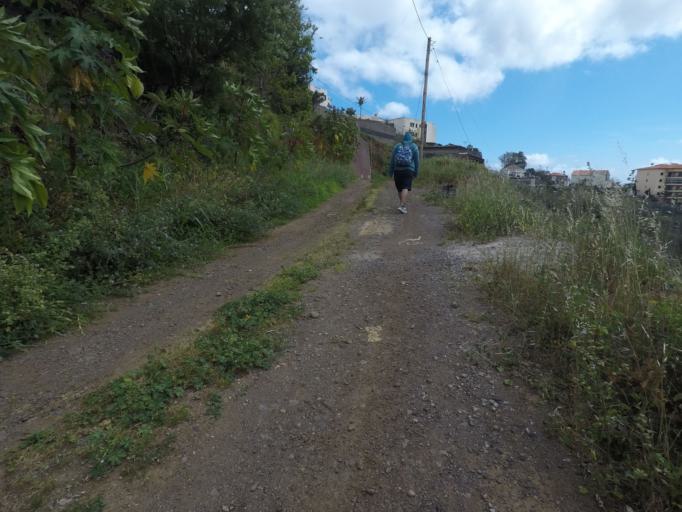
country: PT
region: Madeira
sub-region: Calheta
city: Estreito da Calheta
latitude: 32.7285
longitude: -17.1802
